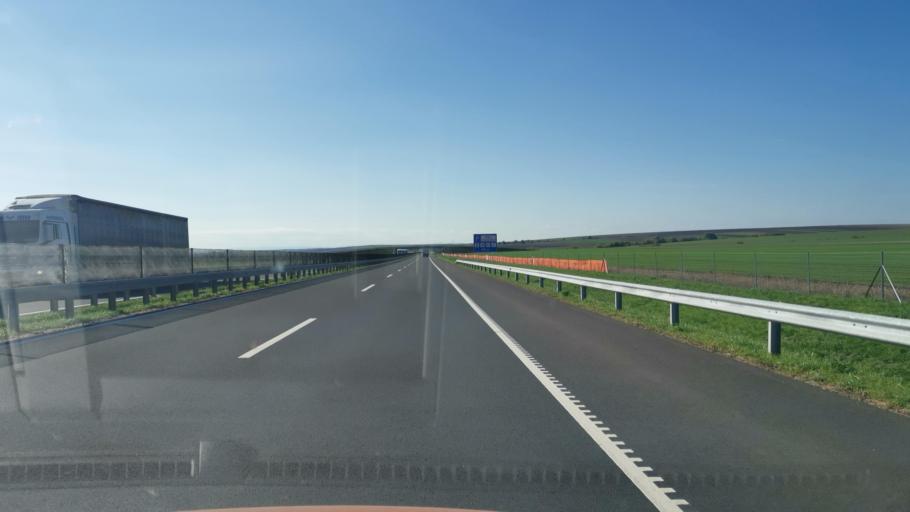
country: HU
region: Borsod-Abauj-Zemplen
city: Halmaj
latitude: 48.2987
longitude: 21.0501
